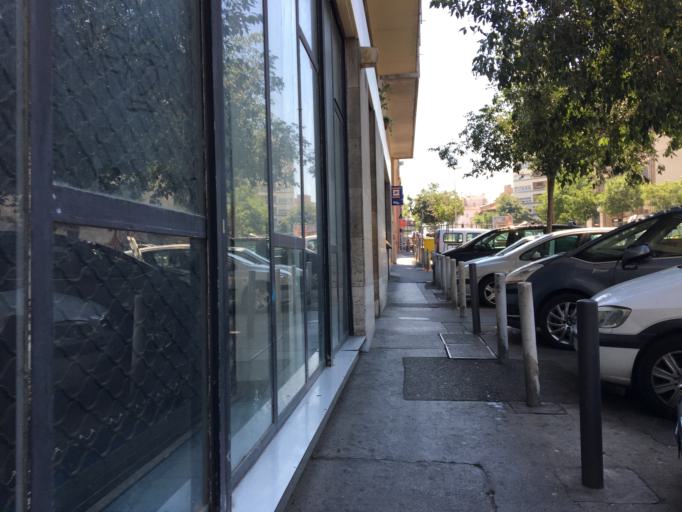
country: FR
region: Provence-Alpes-Cote d'Azur
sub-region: Departement des Bouches-du-Rhone
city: Marseille 03
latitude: 43.3060
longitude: 5.3722
